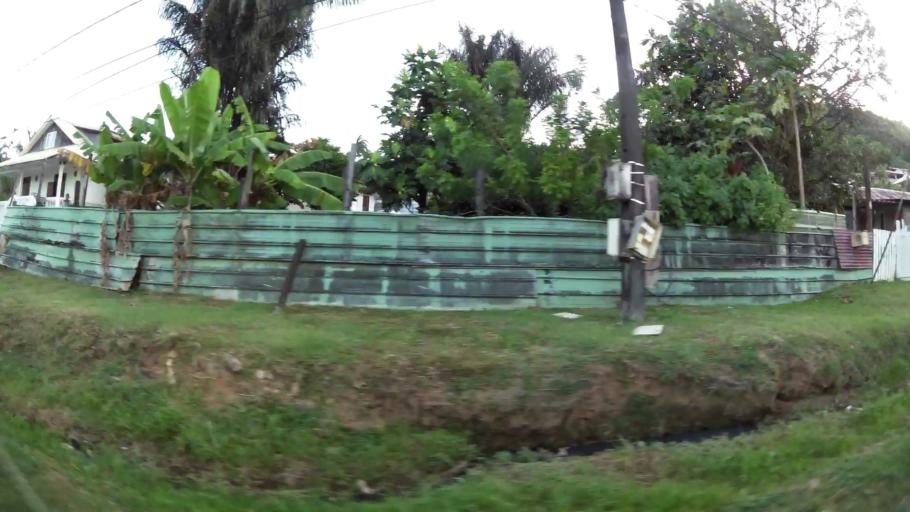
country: GF
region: Guyane
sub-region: Guyane
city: Cayenne
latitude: 4.9218
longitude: -52.3046
